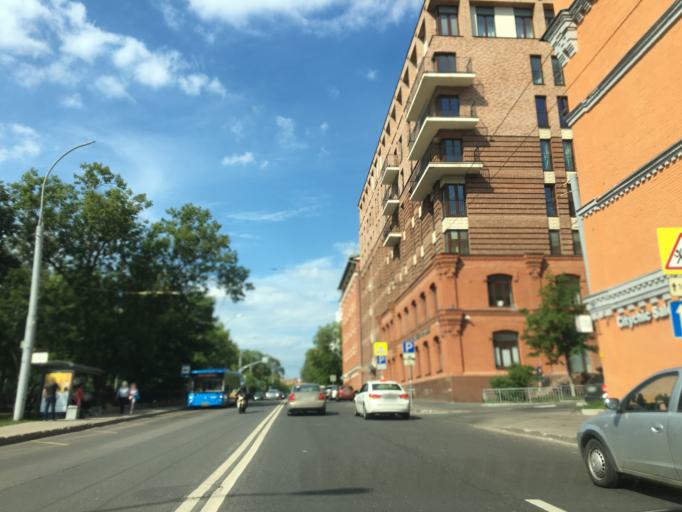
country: RU
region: Moskovskaya
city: Dorogomilovo
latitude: 55.7597
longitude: 37.5605
